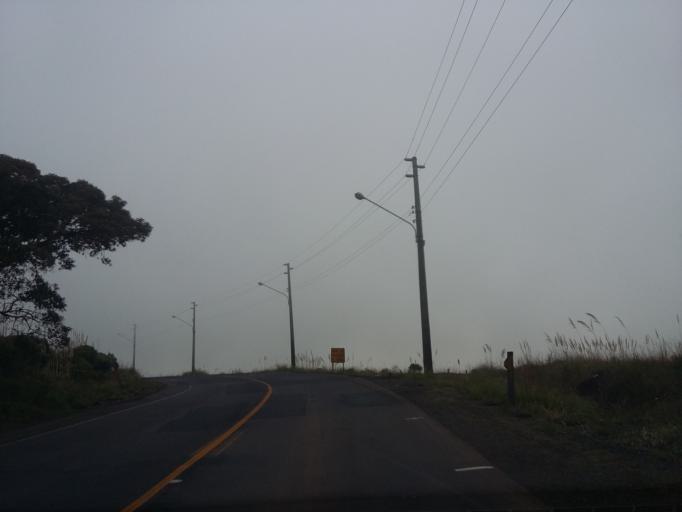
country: BR
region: Santa Catarina
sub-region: Lauro Muller
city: Lauro Muller
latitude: -28.3966
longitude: -49.5516
